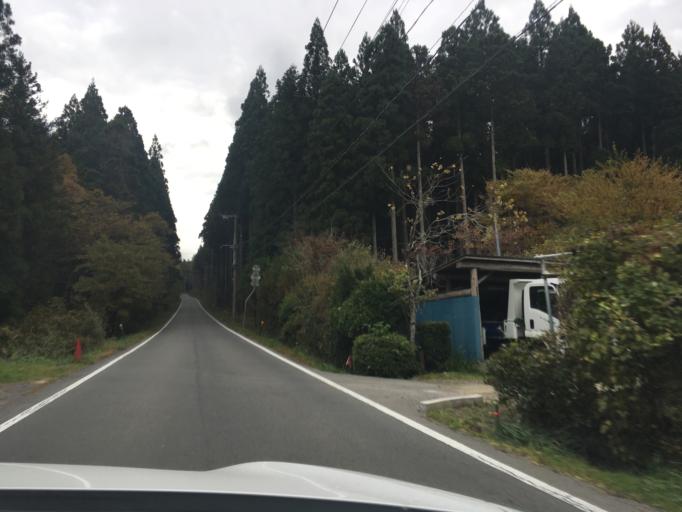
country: JP
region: Fukushima
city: Iwaki
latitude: 37.1138
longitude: 140.7790
